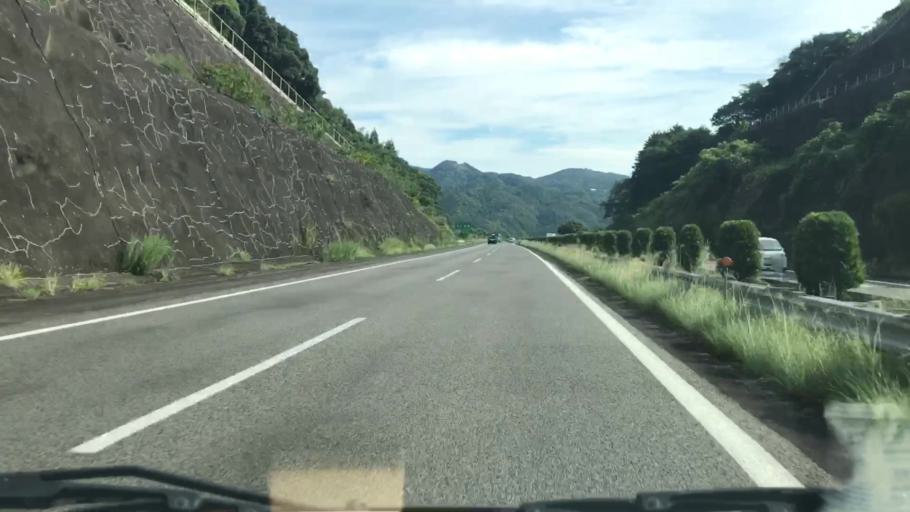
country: JP
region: Saga Prefecture
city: Takeocho-takeo
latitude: 33.2793
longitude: 130.1184
